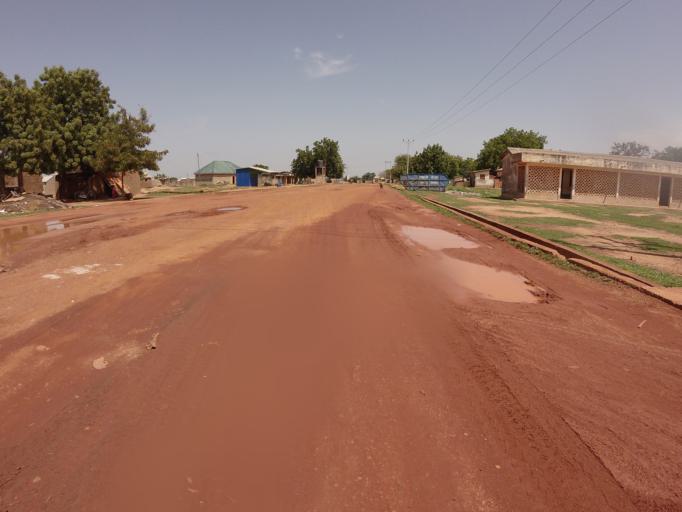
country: GH
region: Upper East
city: Bawku
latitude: 11.1464
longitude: -0.2090
